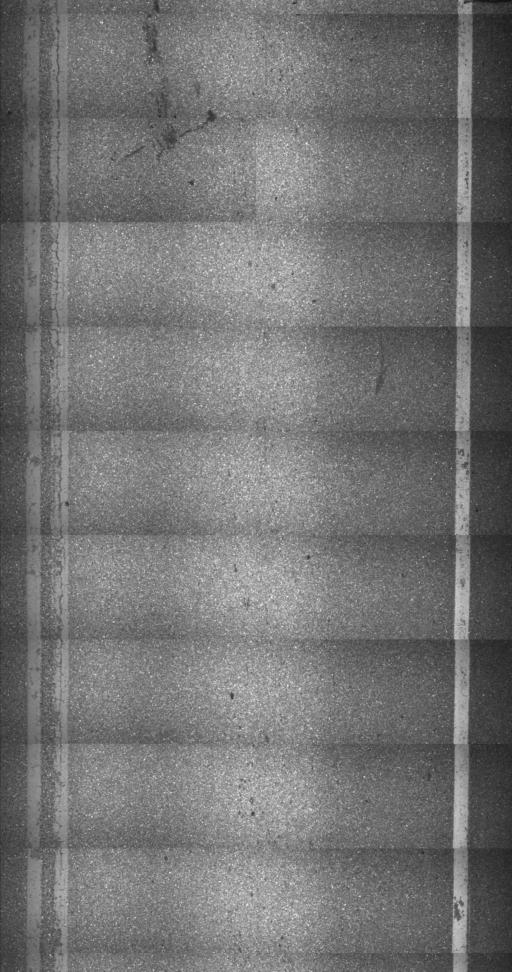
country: US
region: Vermont
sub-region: Orange County
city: Randolph
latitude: 43.9191
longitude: -72.8400
